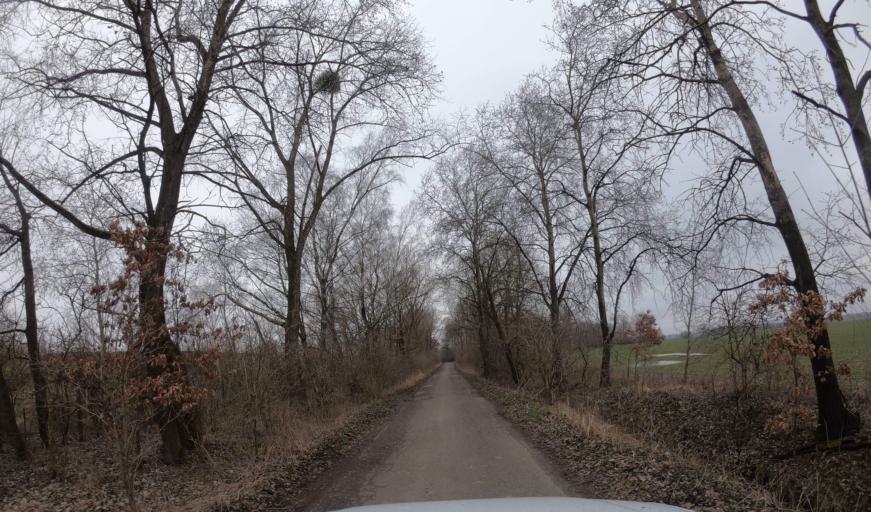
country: PL
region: West Pomeranian Voivodeship
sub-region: Powiat gryficki
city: Ploty
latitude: 53.8594
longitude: 15.2620
